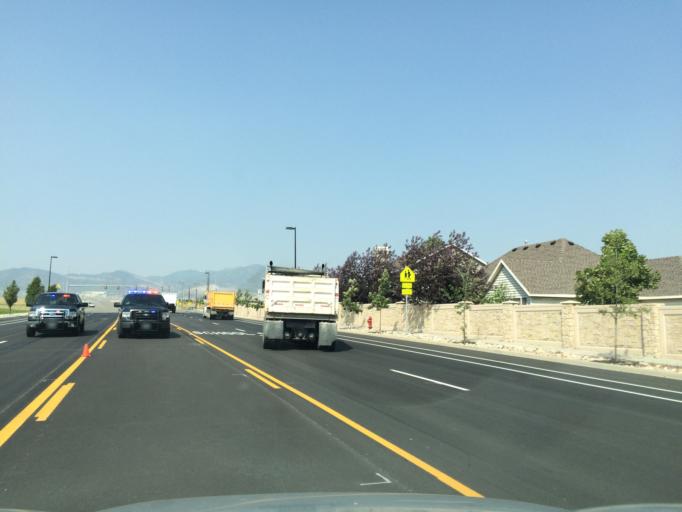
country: US
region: Utah
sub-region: Salt Lake County
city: Oquirrh
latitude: 40.5879
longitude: -112.0215
